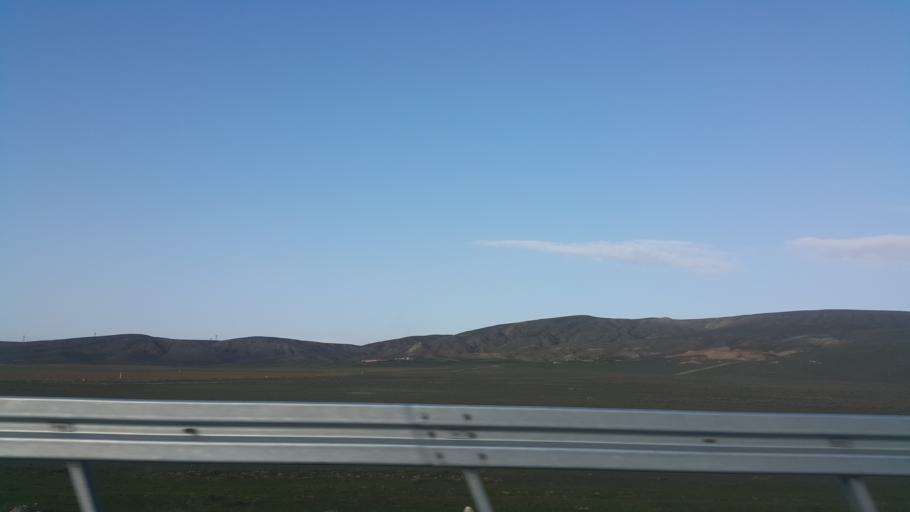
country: TR
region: Konya
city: Kulu
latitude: 39.1396
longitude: 33.3391
